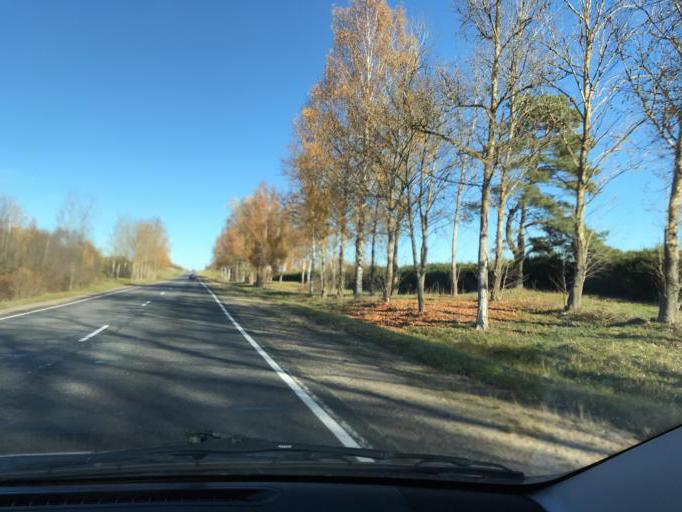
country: BY
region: Vitebsk
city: Lyepyel'
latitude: 55.0159
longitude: 28.7414
